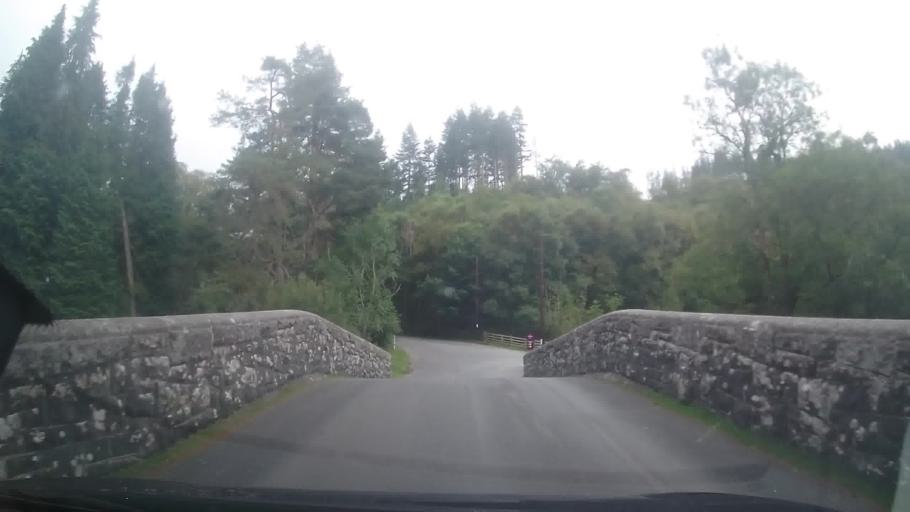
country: GB
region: Wales
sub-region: Sir Powys
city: Rhayader
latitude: 52.2938
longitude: -3.5912
